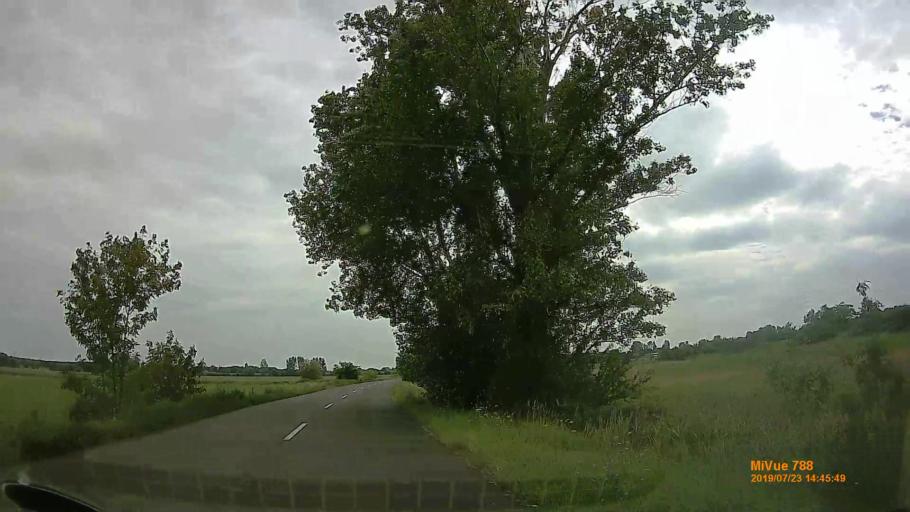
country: HU
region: Szabolcs-Szatmar-Bereg
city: Nyiregyhaza
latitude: 47.9253
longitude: 21.6774
